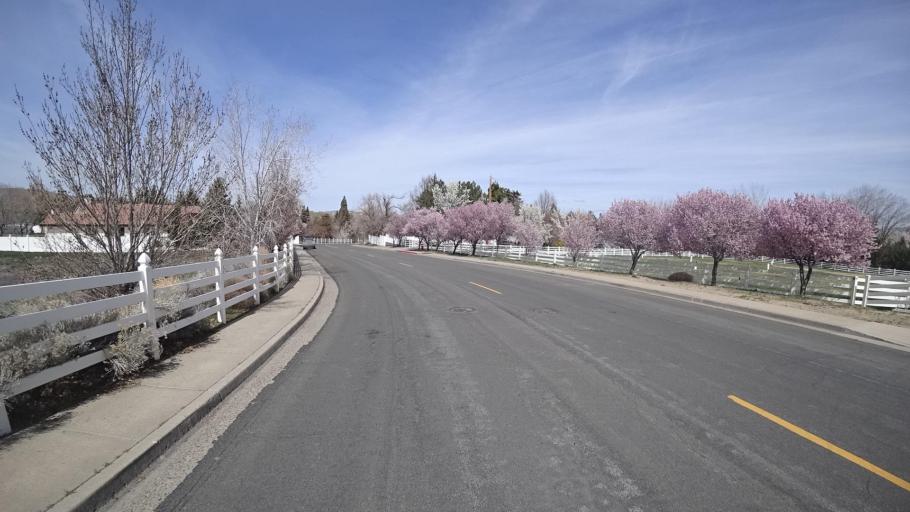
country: US
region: Nevada
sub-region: Washoe County
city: Reno
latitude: 39.4898
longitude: -119.8222
